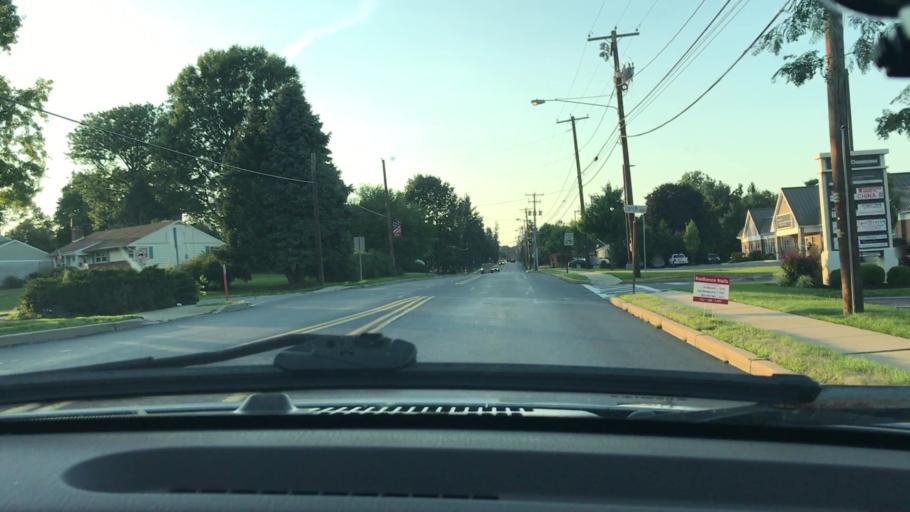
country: US
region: Pennsylvania
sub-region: Lancaster County
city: East Petersburg
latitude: 40.0942
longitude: -76.3510
